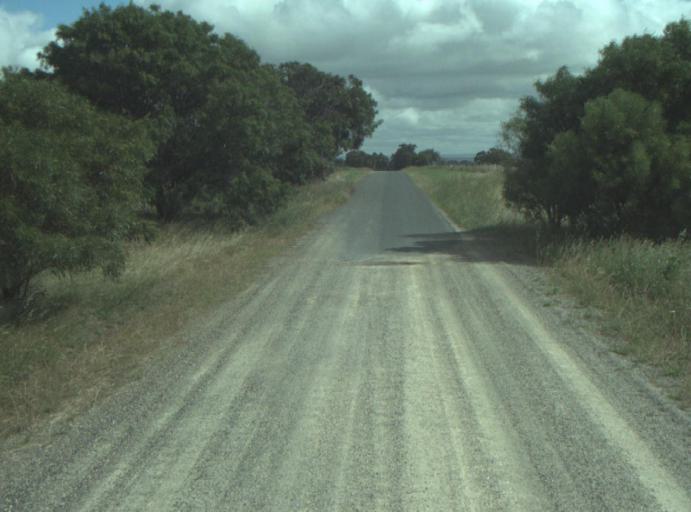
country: AU
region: Victoria
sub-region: Greater Geelong
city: Lara
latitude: -37.8648
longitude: 144.3244
